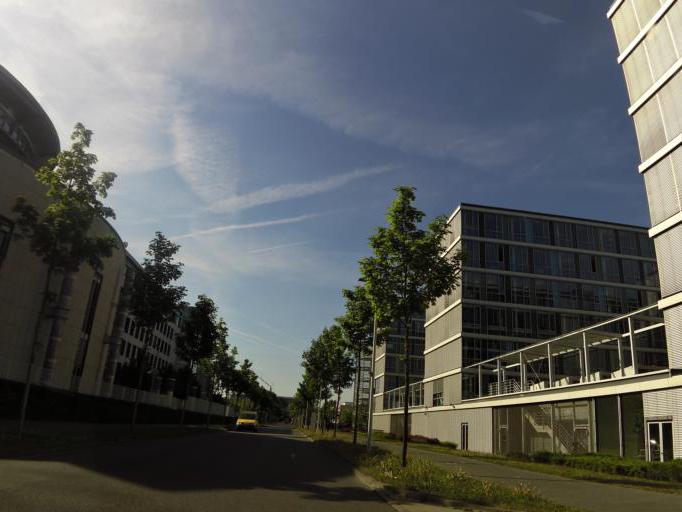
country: DE
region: Hesse
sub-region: Regierungsbezirk Darmstadt
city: Darmstadt
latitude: 49.8651
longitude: 8.6262
